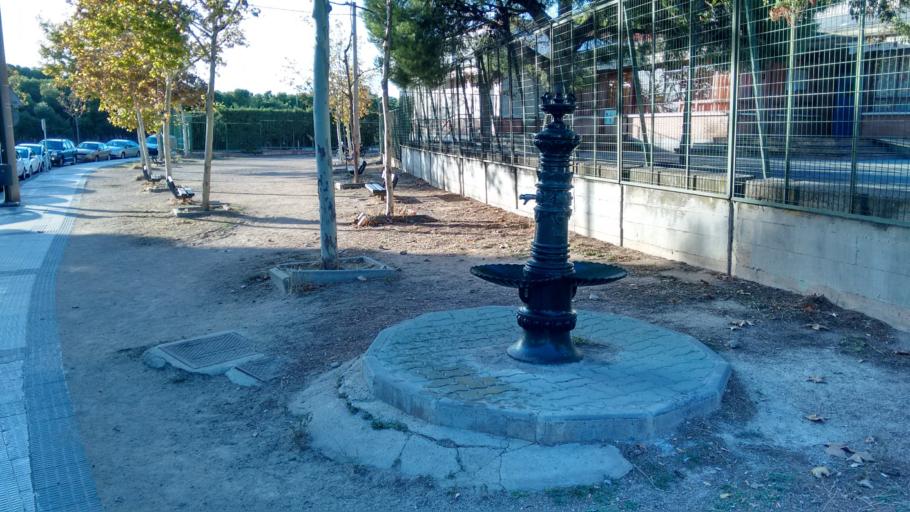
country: ES
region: Aragon
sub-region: Provincia de Zaragoza
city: Zaragoza
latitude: 41.6248
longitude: -0.8808
